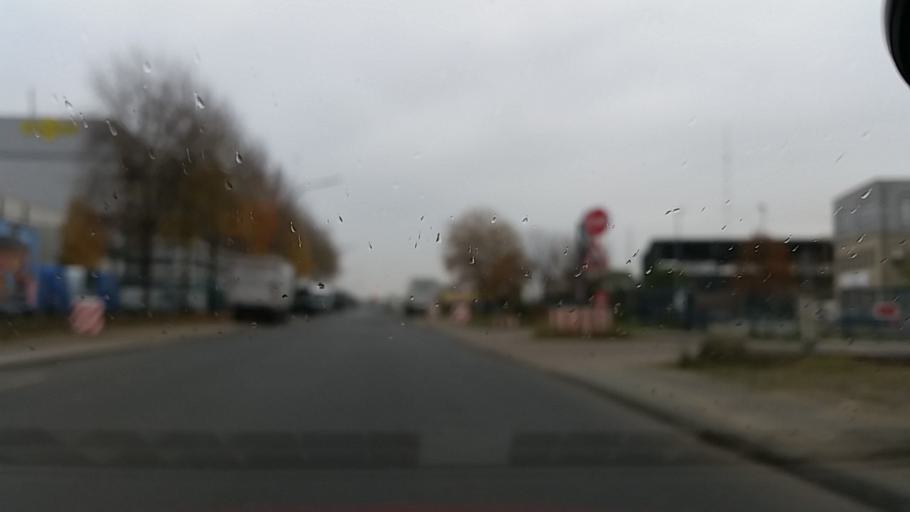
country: DE
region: Hamburg
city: Marienthal
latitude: 53.5270
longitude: 10.0887
